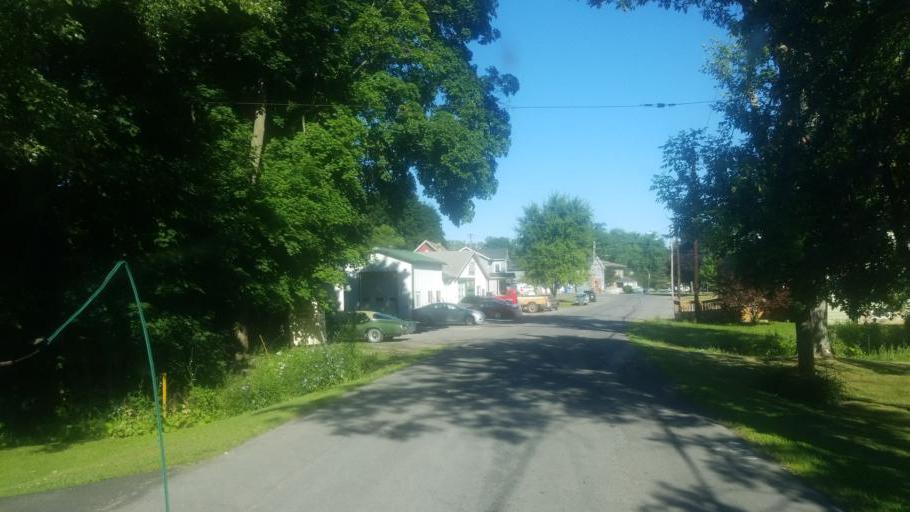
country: US
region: New York
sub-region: Ontario County
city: Phelps
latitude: 42.8865
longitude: -77.0944
